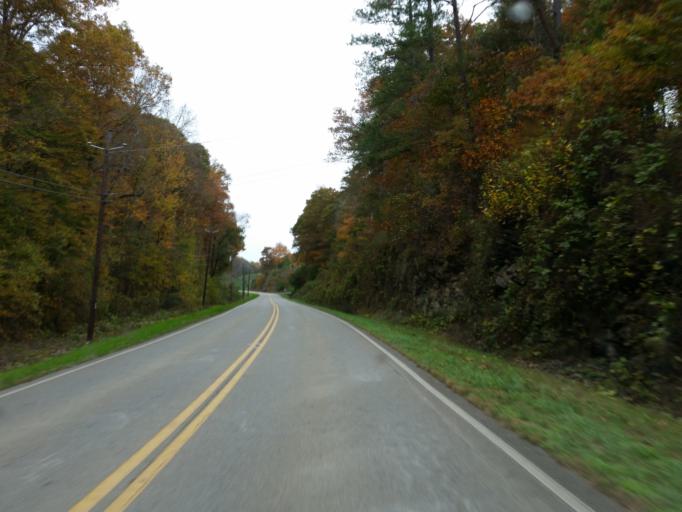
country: US
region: Georgia
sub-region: Pickens County
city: Jasper
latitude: 34.4932
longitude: -84.4270
